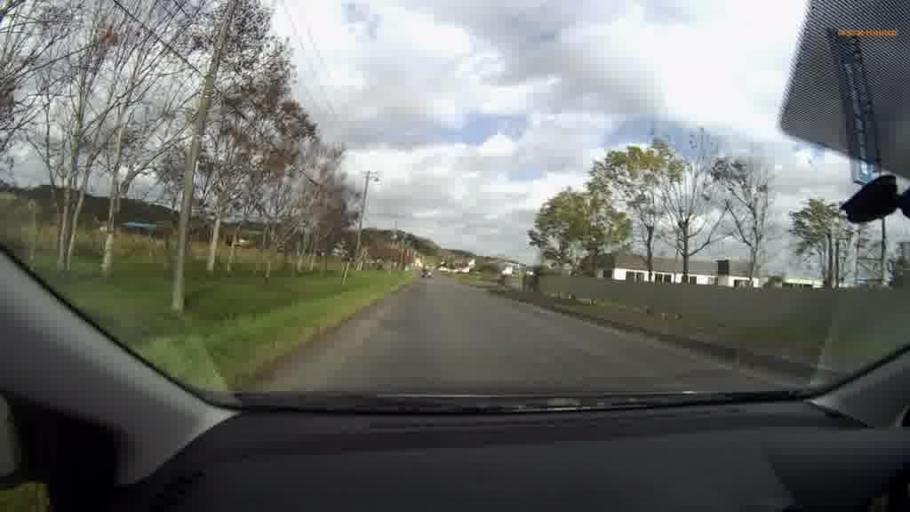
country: JP
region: Hokkaido
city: Kushiro
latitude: 42.9729
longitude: 144.1251
